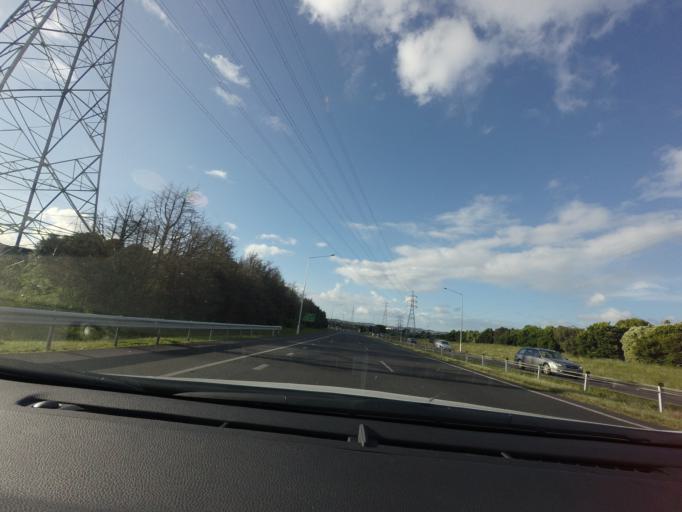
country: NZ
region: Auckland
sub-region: Auckland
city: Papakura
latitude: -37.0639
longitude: 174.9251
